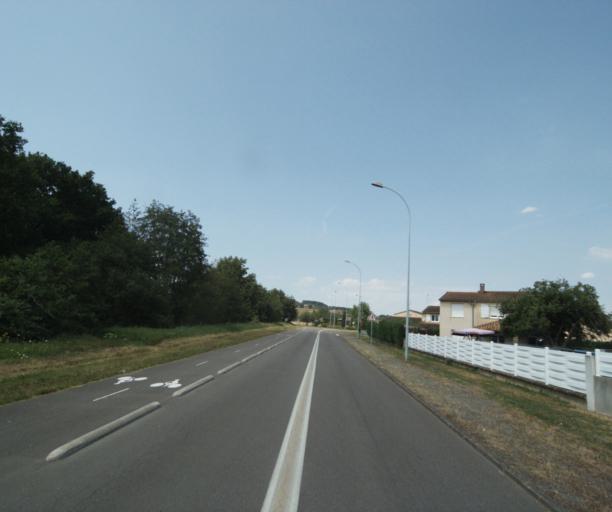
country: FR
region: Bourgogne
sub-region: Departement de Saone-et-Loire
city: Gueugnon
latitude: 46.6060
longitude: 4.0473
